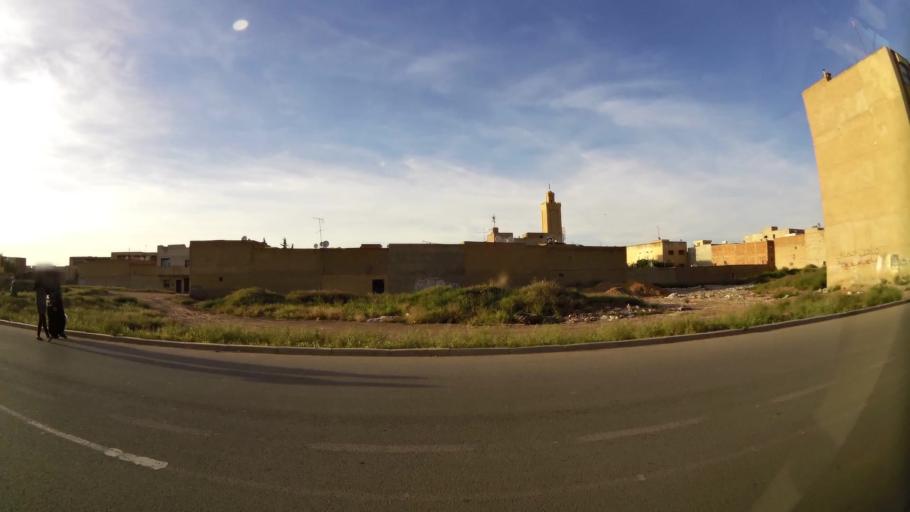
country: MA
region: Oriental
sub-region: Oujda-Angad
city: Oujda
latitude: 34.6779
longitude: -1.8976
